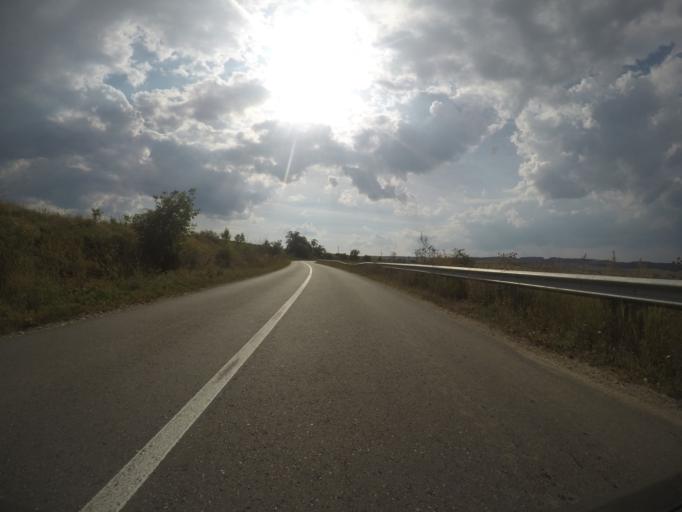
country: RO
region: Cluj
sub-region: Comuna Sandulesti
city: Copaceni
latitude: 46.5874
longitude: 23.7451
